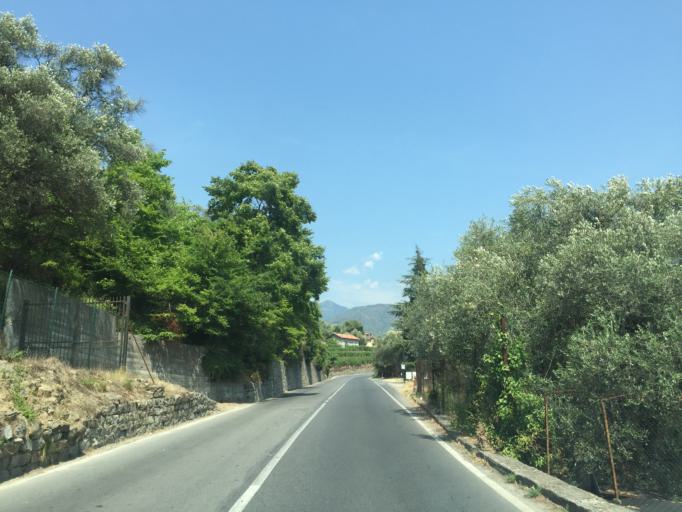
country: IT
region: Liguria
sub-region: Provincia di Imperia
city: Dolceacqua
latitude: 43.8343
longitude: 7.6267
